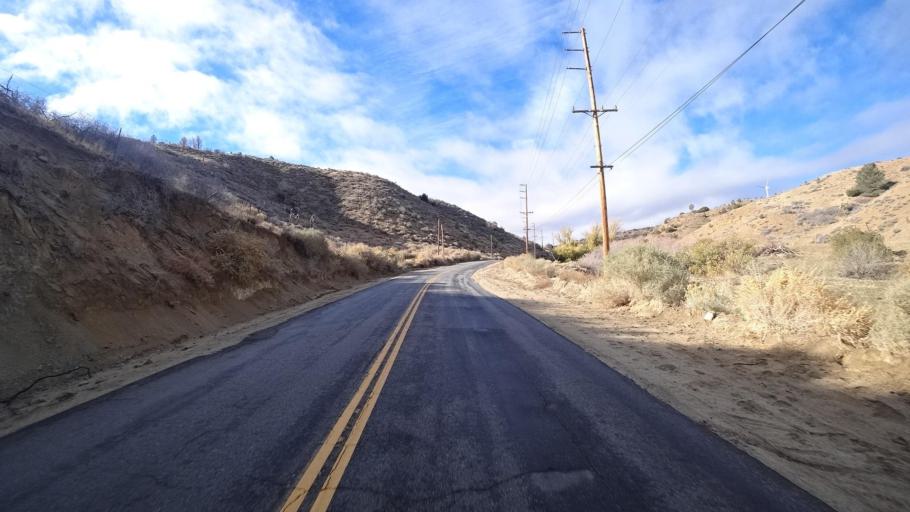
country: US
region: California
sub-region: Kern County
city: Tehachapi
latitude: 35.0886
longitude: -118.3143
